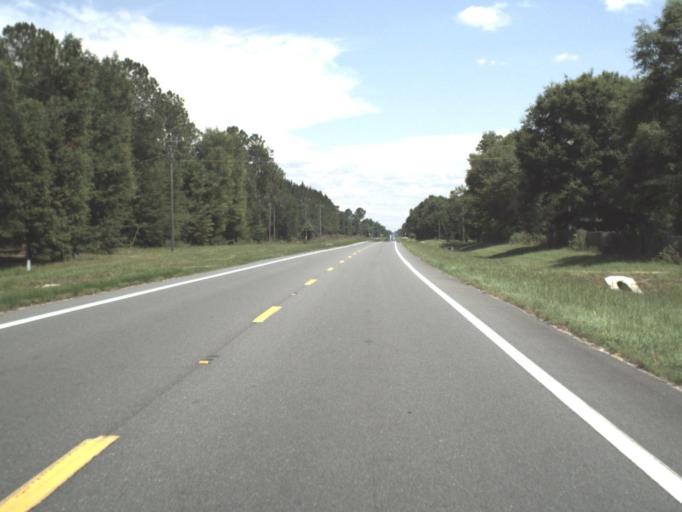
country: US
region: Florida
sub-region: Lafayette County
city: Mayo
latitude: 30.1210
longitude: -83.2648
